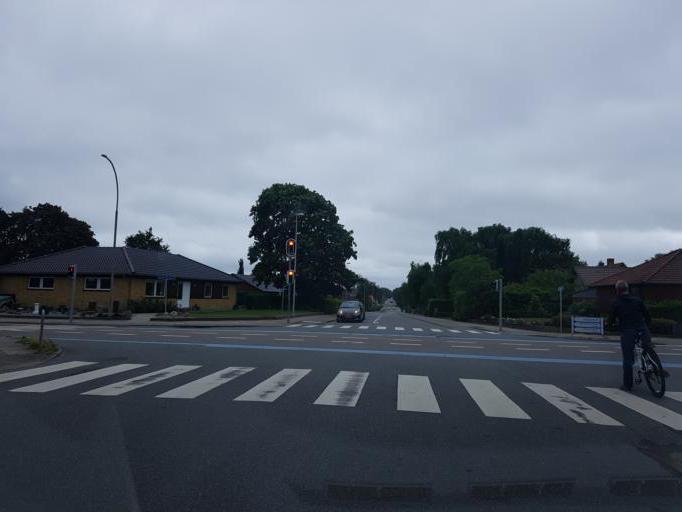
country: DK
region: South Denmark
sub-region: Varde Kommune
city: Varde
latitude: 55.6310
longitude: 8.4901
